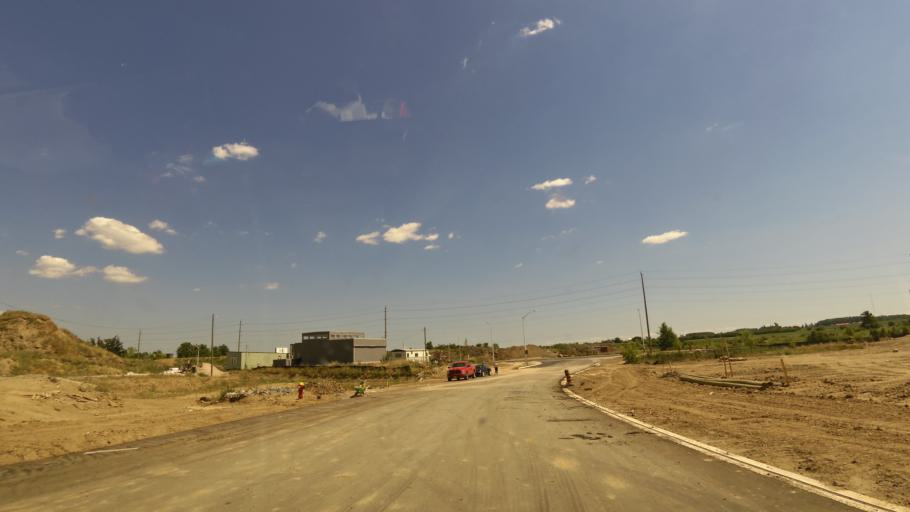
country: CA
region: Ontario
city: Brampton
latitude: 43.6345
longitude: -79.8683
